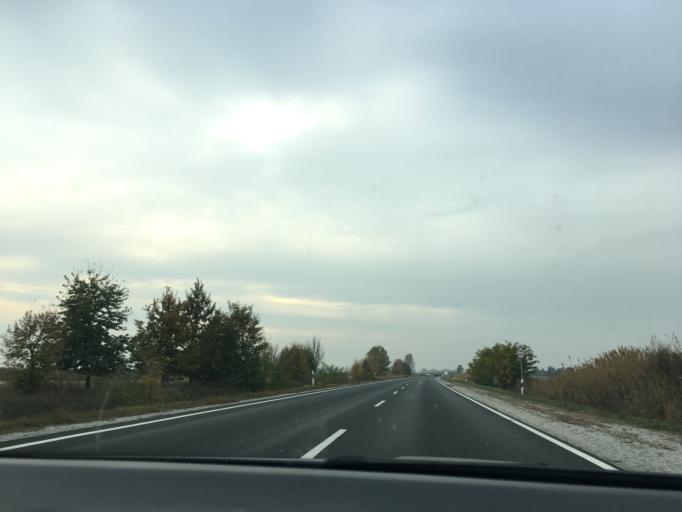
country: HU
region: Pest
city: Abony
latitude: 47.1999
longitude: 19.9482
